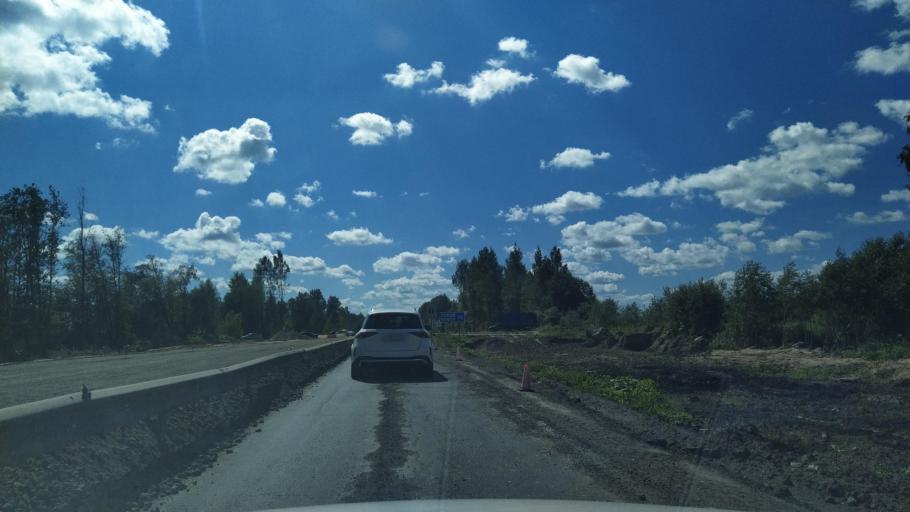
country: RU
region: Leningrad
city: Luga
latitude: 58.6154
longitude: 29.8303
